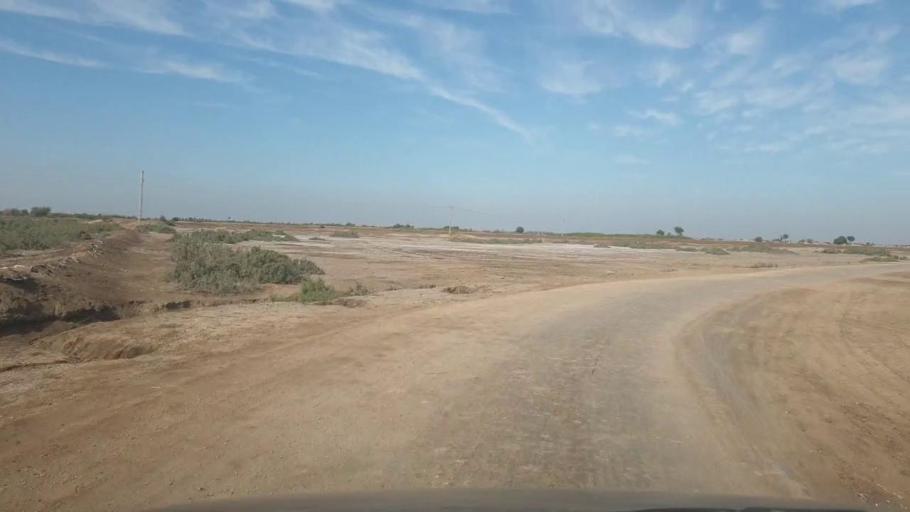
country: PK
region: Sindh
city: Pithoro
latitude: 25.4384
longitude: 69.2033
